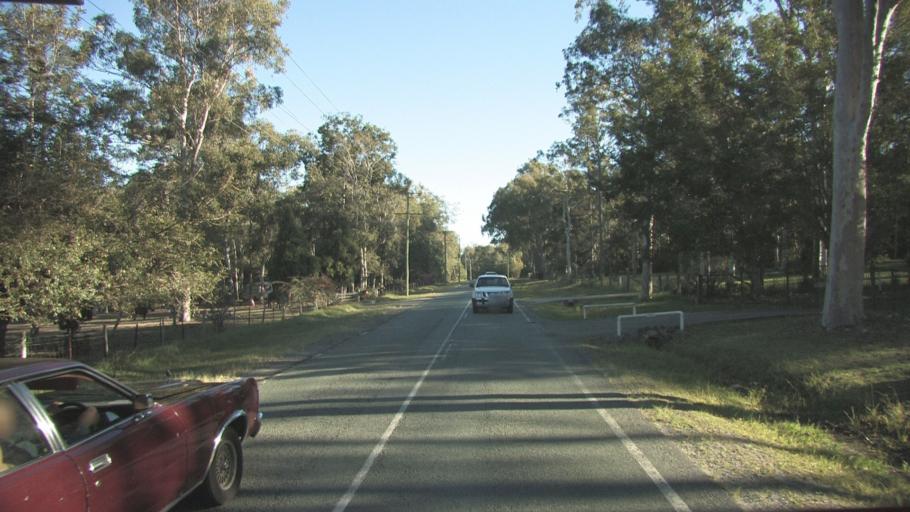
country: AU
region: Queensland
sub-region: Logan
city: Chambers Flat
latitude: -27.7531
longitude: 153.0520
